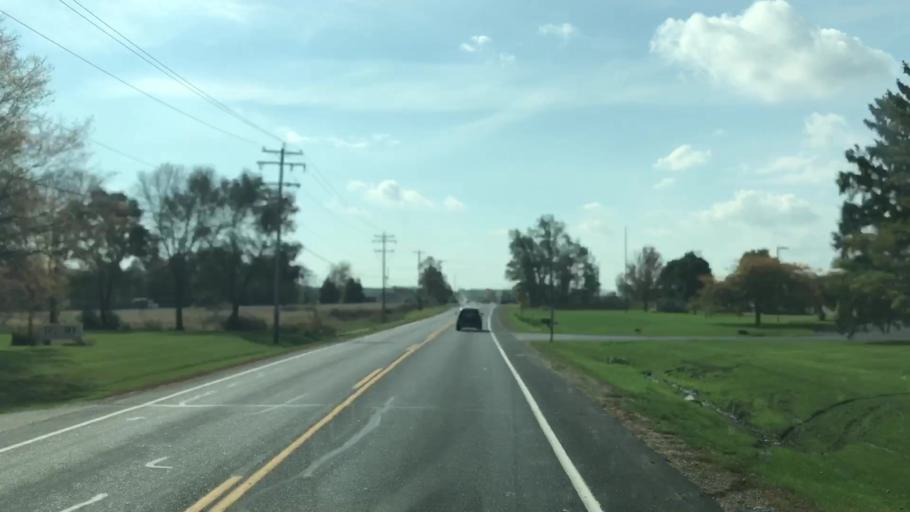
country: US
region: Wisconsin
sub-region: Ozaukee County
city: Mequon
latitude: 43.1947
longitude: -88.0436
